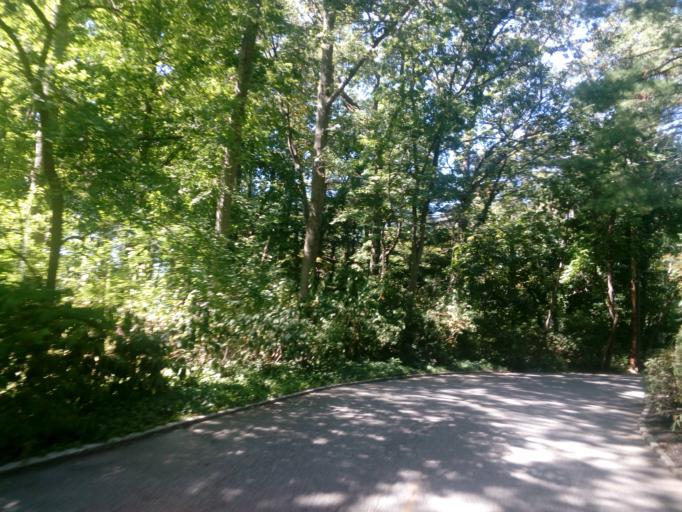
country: US
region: New York
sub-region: Nassau County
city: Upper Brookville
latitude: 40.8456
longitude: -73.5652
